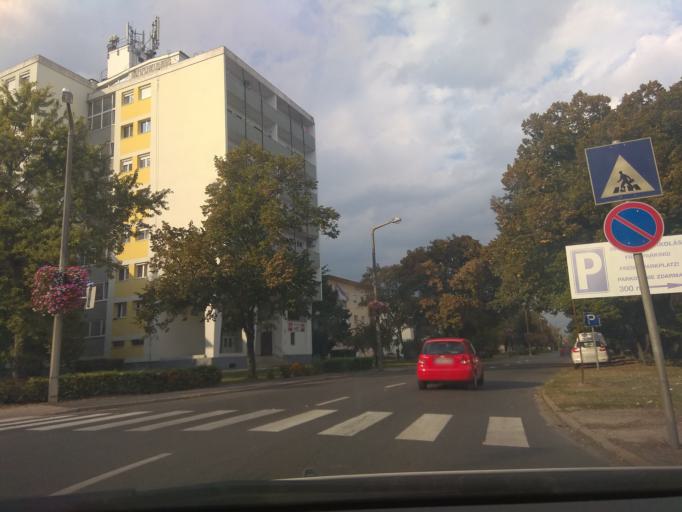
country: HU
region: Borsod-Abauj-Zemplen
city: Sajooeroes
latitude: 47.9271
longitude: 21.0429
